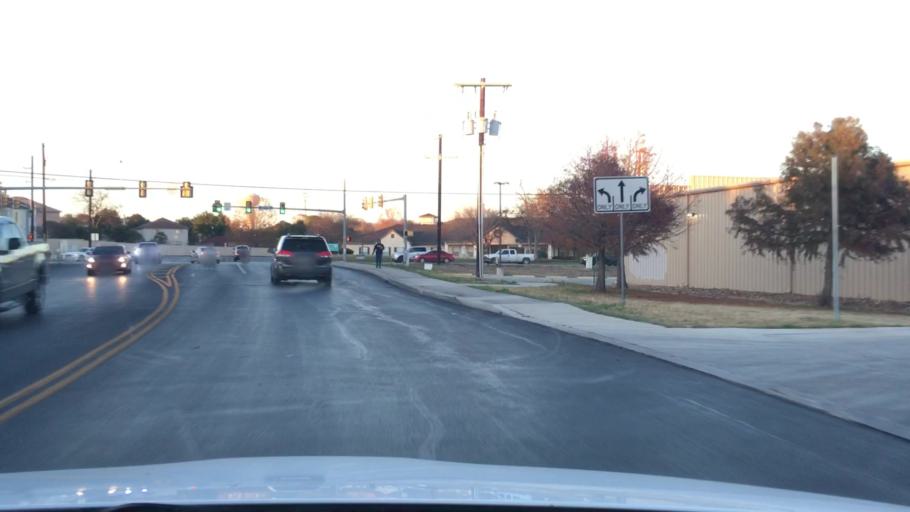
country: US
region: Texas
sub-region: Bexar County
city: Windcrest
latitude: 29.5208
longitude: -98.3545
